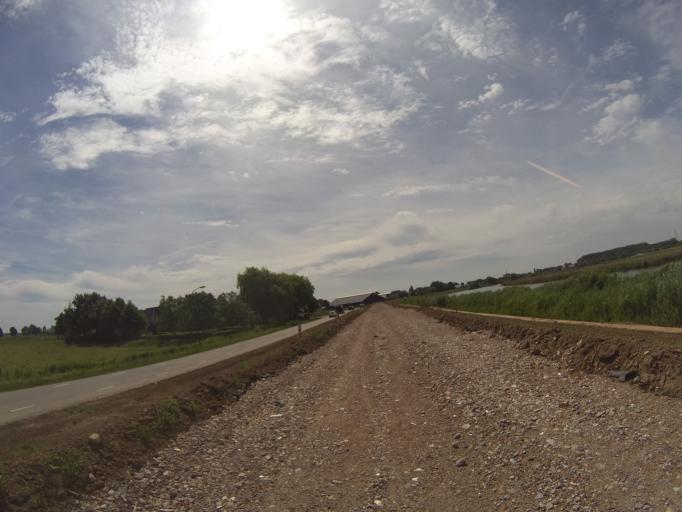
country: NL
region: Utrecht
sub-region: Gemeente Baarn
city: Baarn
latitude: 52.2369
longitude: 5.3132
